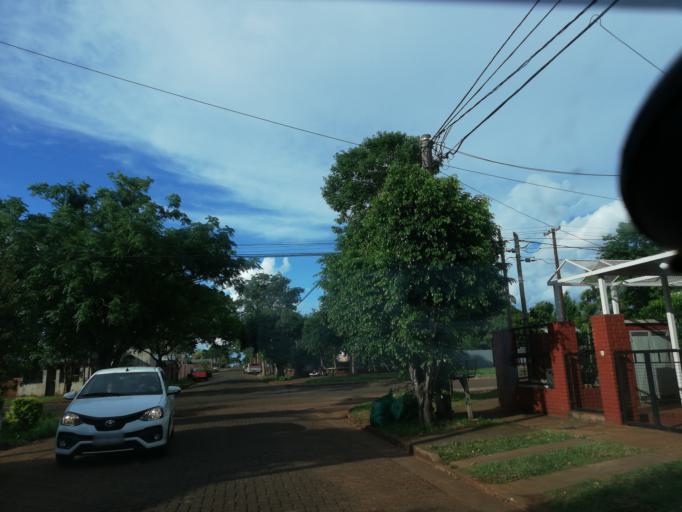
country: AR
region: Misiones
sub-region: Departamento de Capital
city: Posadas
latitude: -27.4161
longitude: -55.9514
